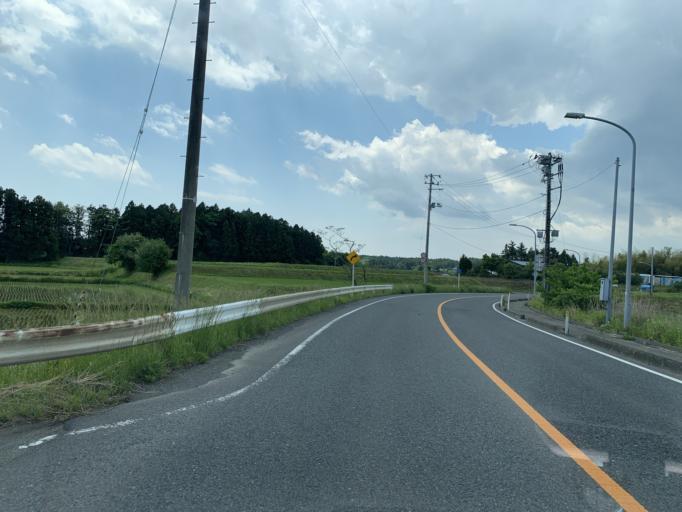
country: JP
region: Miyagi
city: Matsushima
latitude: 38.4381
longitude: 141.0706
